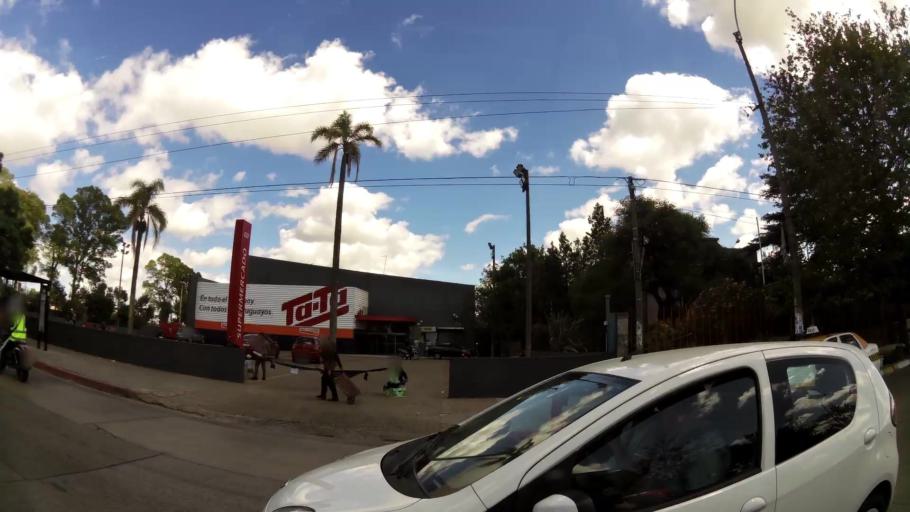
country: UY
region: Canelones
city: Paso de Carrasco
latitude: -34.8410
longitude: -56.1234
